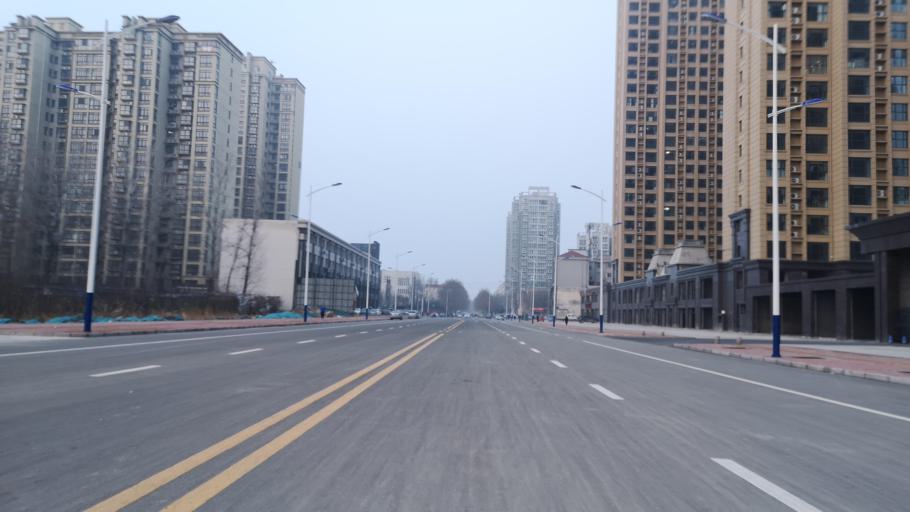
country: CN
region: Henan Sheng
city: Zhongyuanlu
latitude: 35.7510
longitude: 115.0602
